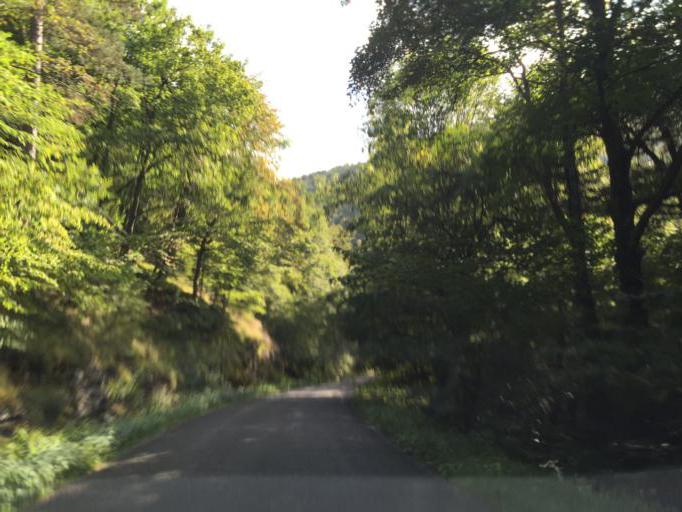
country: FR
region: Rhone-Alpes
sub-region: Departement de la Loire
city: Saint-Jean-Bonnefonds
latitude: 45.4179
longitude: 4.4478
